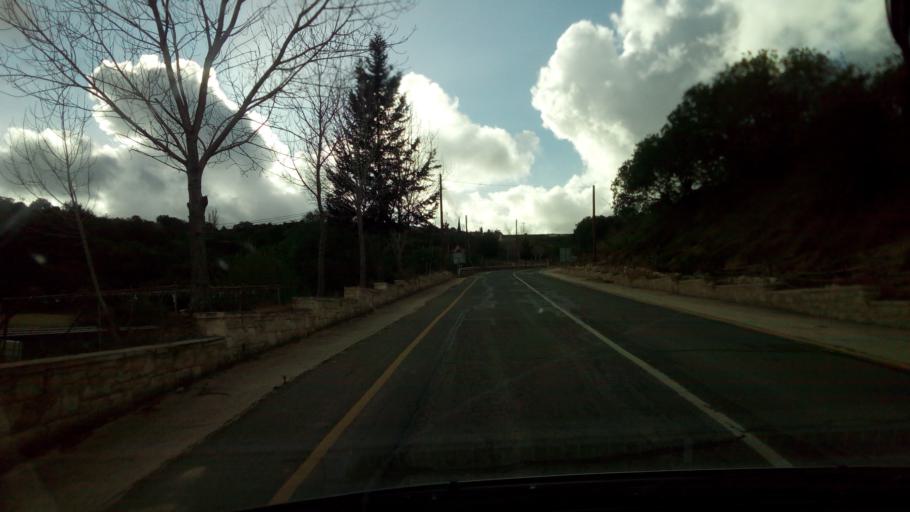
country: CY
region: Pafos
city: Mesogi
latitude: 34.8579
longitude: 32.5068
